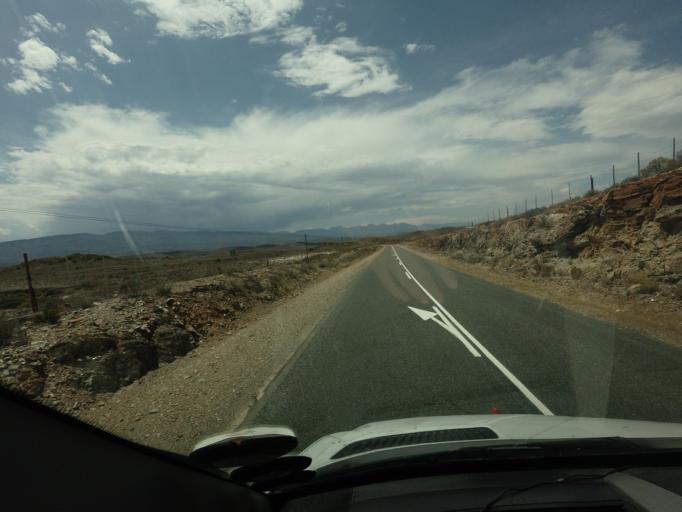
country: ZA
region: Western Cape
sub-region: Eden District Municipality
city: Ladismith
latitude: -33.6935
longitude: 20.9661
